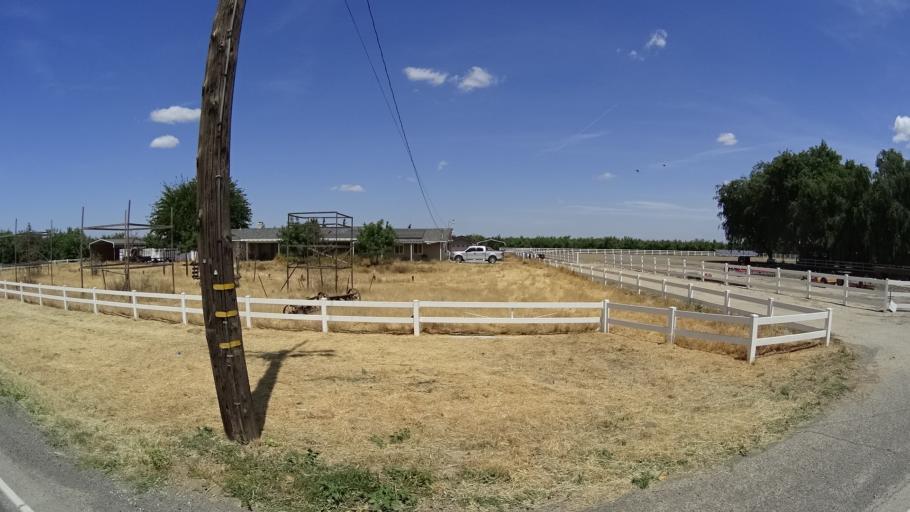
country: US
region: California
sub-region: Kings County
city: Armona
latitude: 36.2986
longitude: -119.7361
